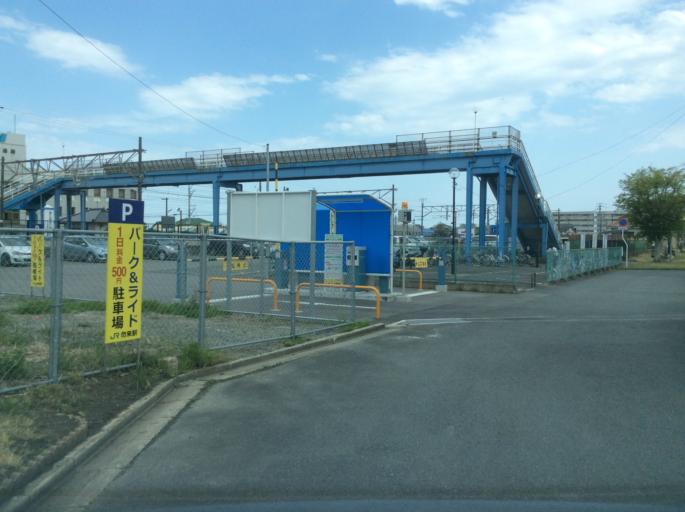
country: JP
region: Ibaraki
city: Kitaibaraki
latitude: 36.8837
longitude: 140.7865
